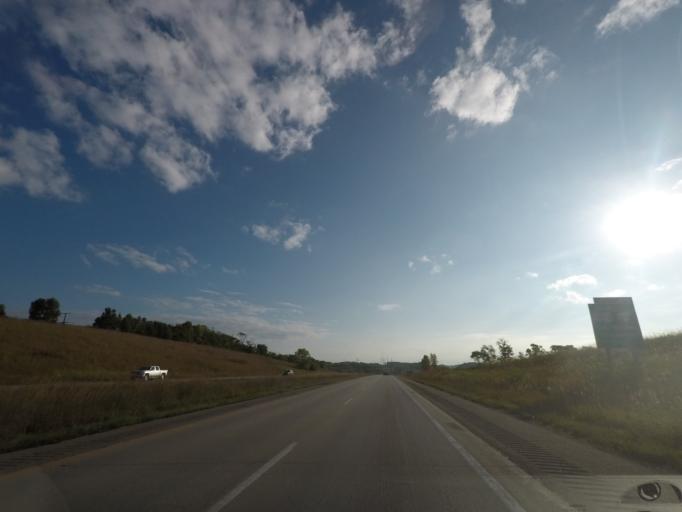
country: US
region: Iowa
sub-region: Warren County
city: Norwalk
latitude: 41.5006
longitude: -93.5984
